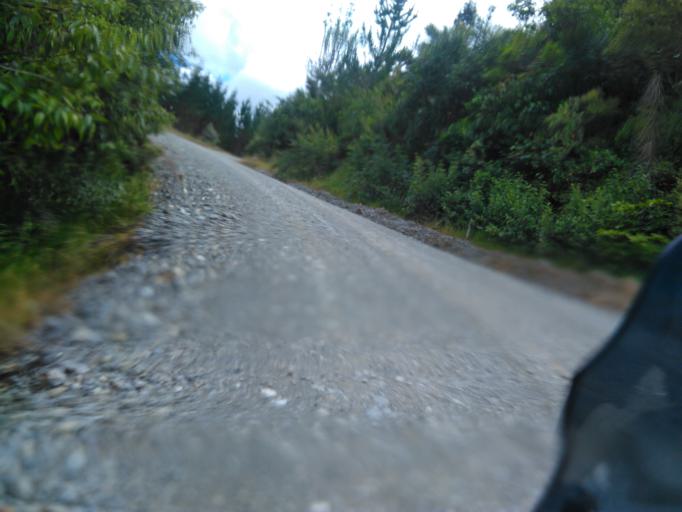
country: NZ
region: Gisborne
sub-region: Gisborne District
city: Gisborne
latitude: -38.1795
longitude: 178.1254
